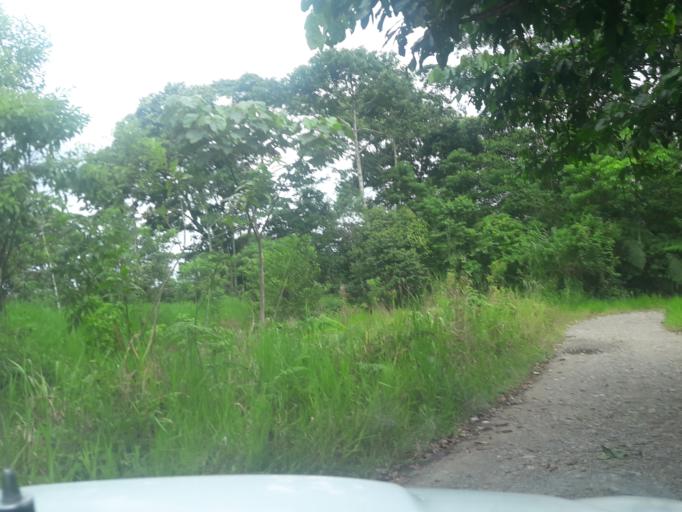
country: EC
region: Napo
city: Tena
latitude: -0.9563
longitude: -77.8142
